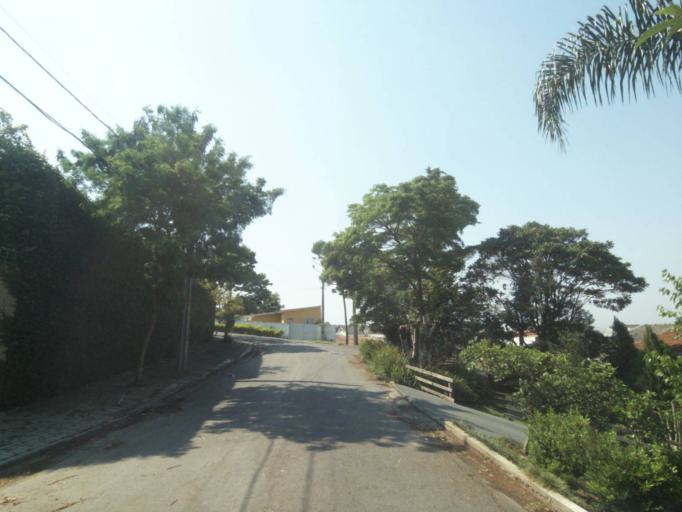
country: BR
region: Parana
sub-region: Sao Jose Dos Pinhais
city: Sao Jose dos Pinhais
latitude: -25.5073
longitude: -49.2754
